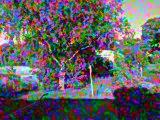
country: SE
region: Soedermanland
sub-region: Flens Kommun
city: Flen
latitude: 59.0689
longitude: 16.5913
